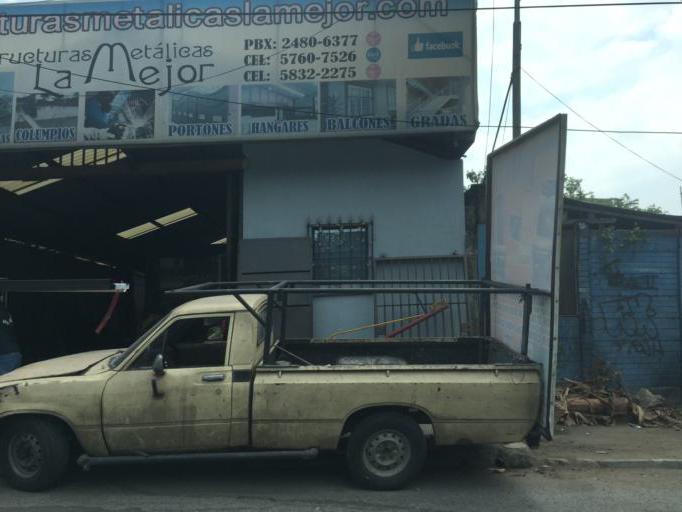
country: GT
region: Guatemala
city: Petapa
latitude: 14.5308
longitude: -90.5543
